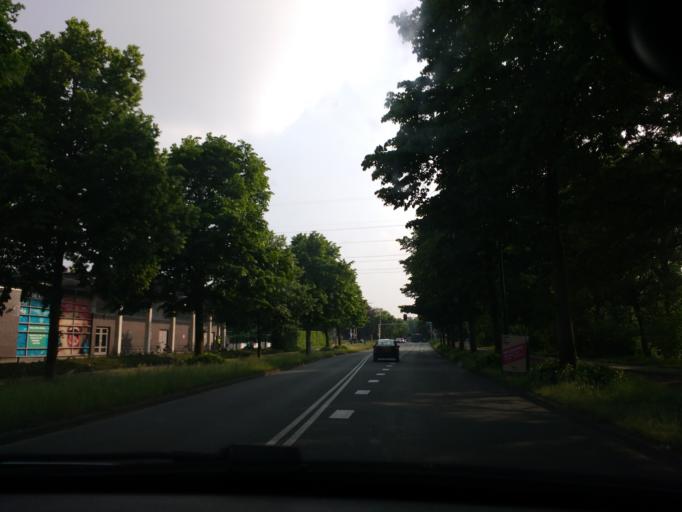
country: NL
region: Utrecht
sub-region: Gemeente Veenendaal
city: Veenendaal
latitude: 52.0269
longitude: 5.5410
